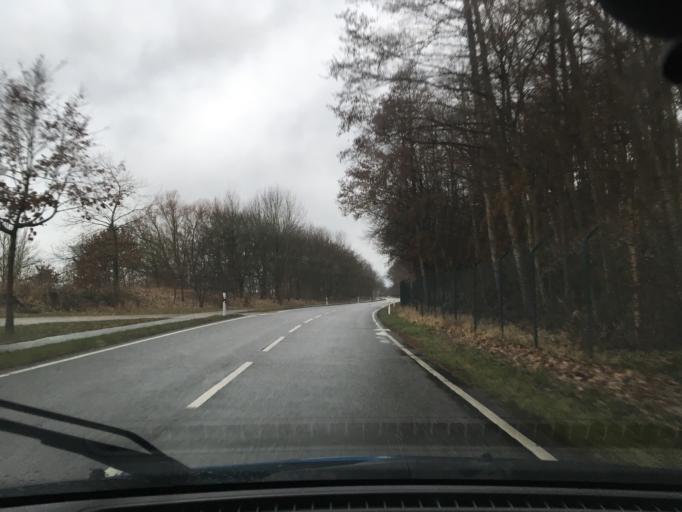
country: DE
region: Lower Saxony
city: Tespe
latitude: 53.4046
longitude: 10.4198
